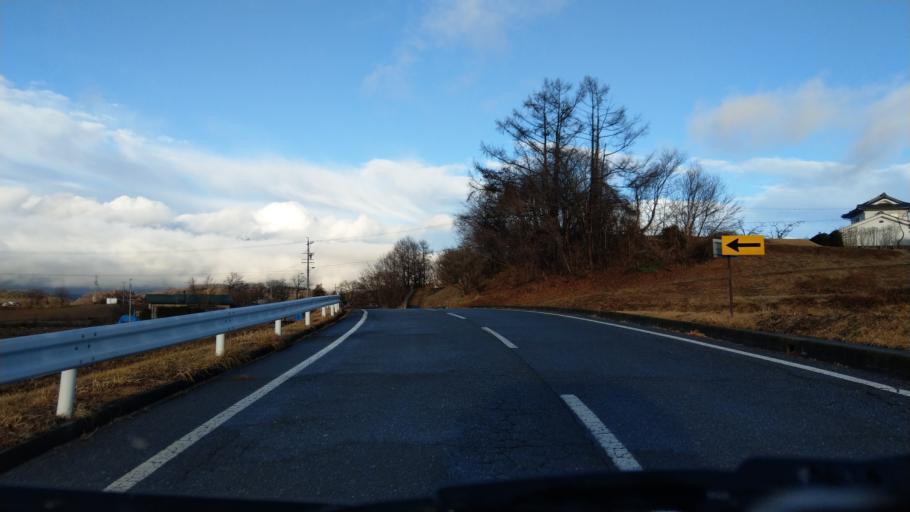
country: JP
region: Nagano
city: Komoro
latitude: 36.3043
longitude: 138.3785
